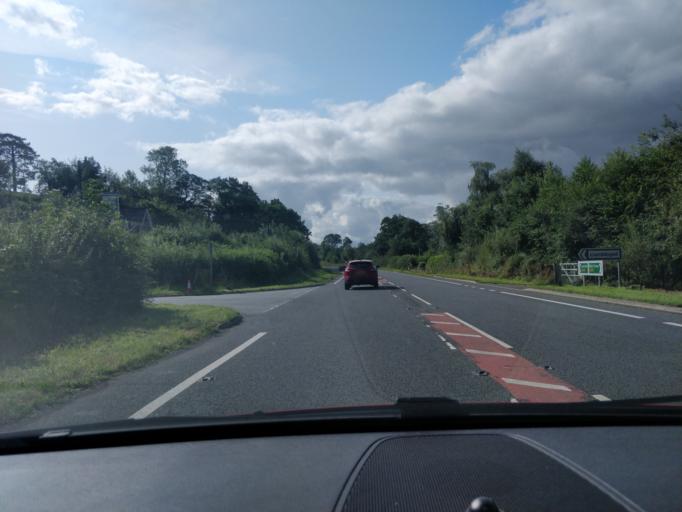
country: GB
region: Wales
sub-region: Conwy
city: Llanrwst
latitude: 53.1559
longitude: -3.8098
